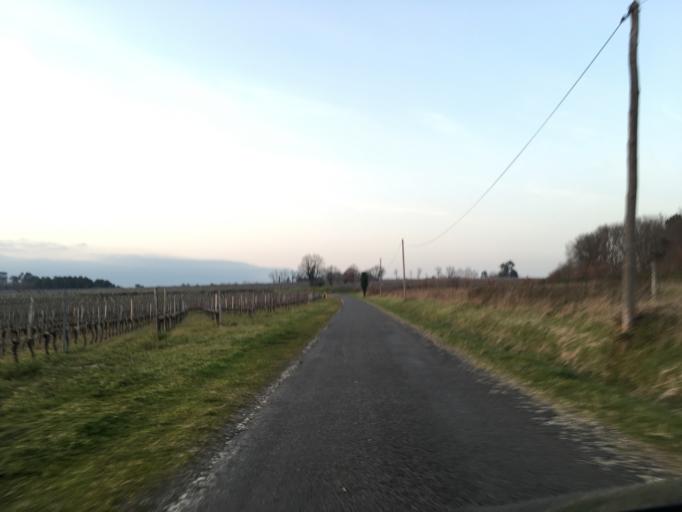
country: FR
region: Aquitaine
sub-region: Departement de la Gironde
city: Saint-Ciers-sur-Gironde
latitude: 45.3009
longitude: -0.6046
